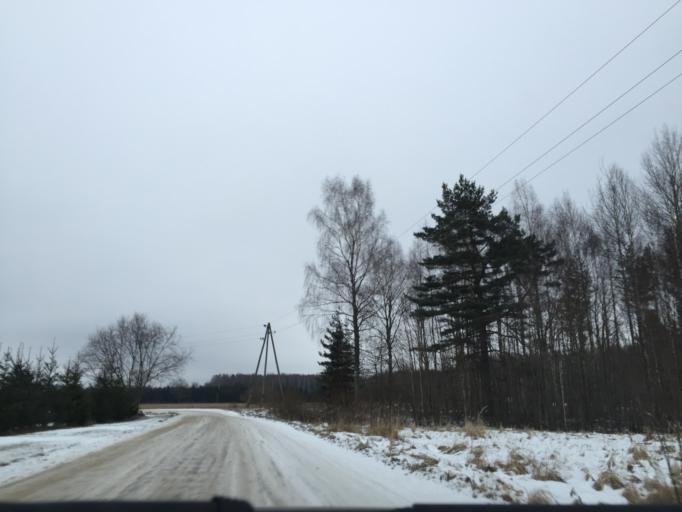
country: LV
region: Saulkrastu
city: Saulkrasti
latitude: 57.2406
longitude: 24.5166
